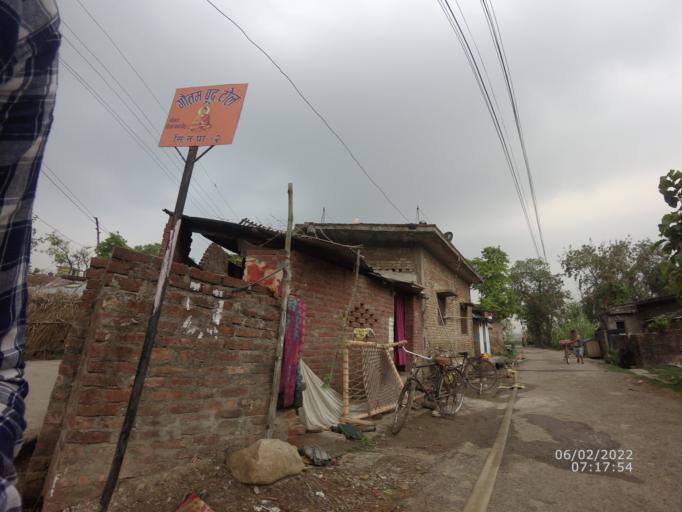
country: NP
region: Western Region
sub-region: Lumbini Zone
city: Bhairahawa
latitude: 27.4840
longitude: 83.4366
